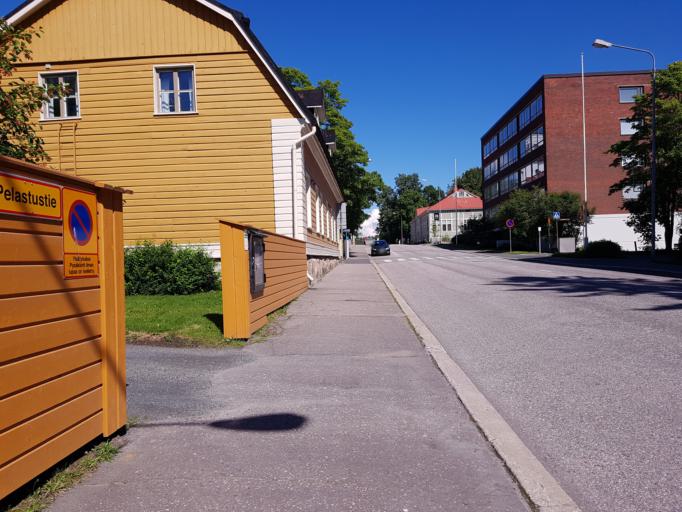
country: FI
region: Northern Savo
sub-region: Kuopio
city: Kuopio
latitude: 62.8896
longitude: 27.6858
